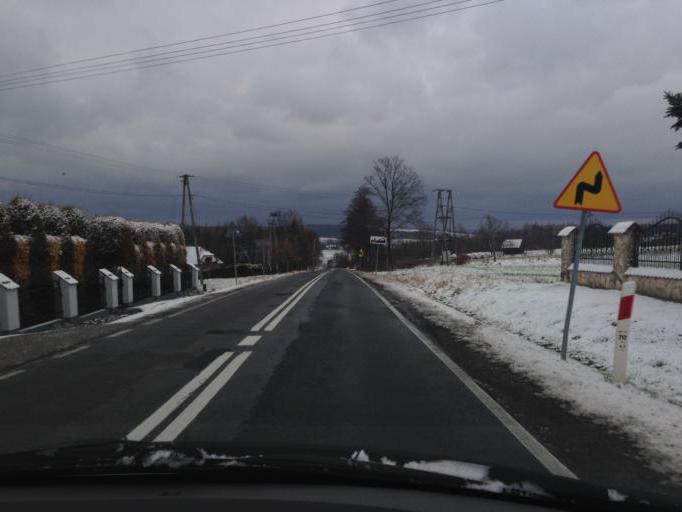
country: PL
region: Lesser Poland Voivodeship
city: Stary Wisnicz
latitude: 49.8502
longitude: 20.5090
